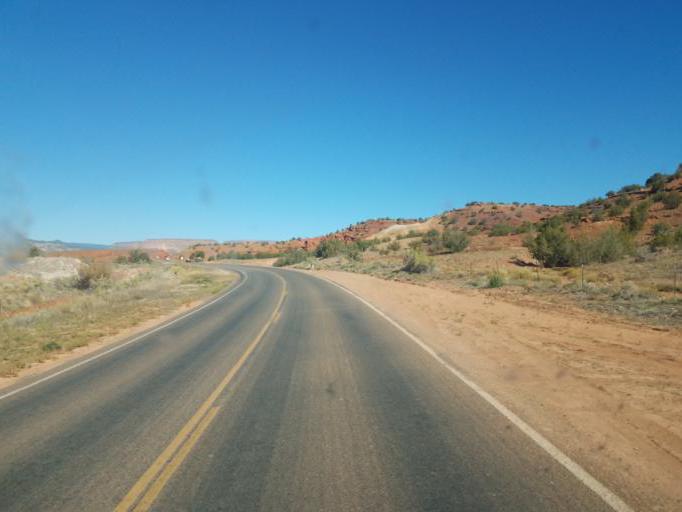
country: US
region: New Mexico
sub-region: Sandoval County
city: Jemez Pueblo
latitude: 35.6355
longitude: -106.7231
